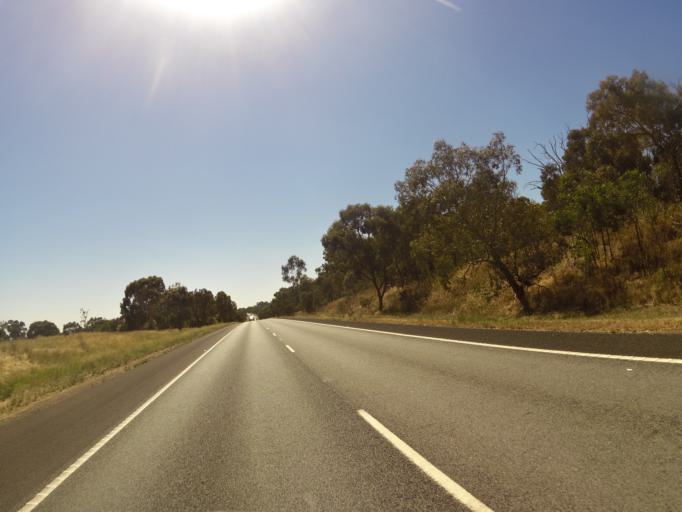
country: AU
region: Victoria
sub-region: Greater Shepparton
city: Shepparton
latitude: -36.8269
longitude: 145.4131
